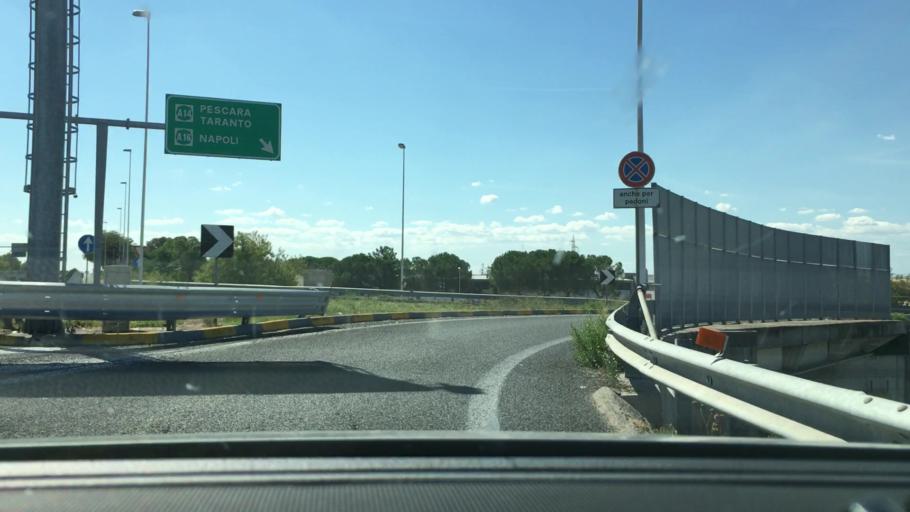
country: IT
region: Apulia
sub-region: Provincia di Bari
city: Bitritto
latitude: 41.0724
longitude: 16.8293
